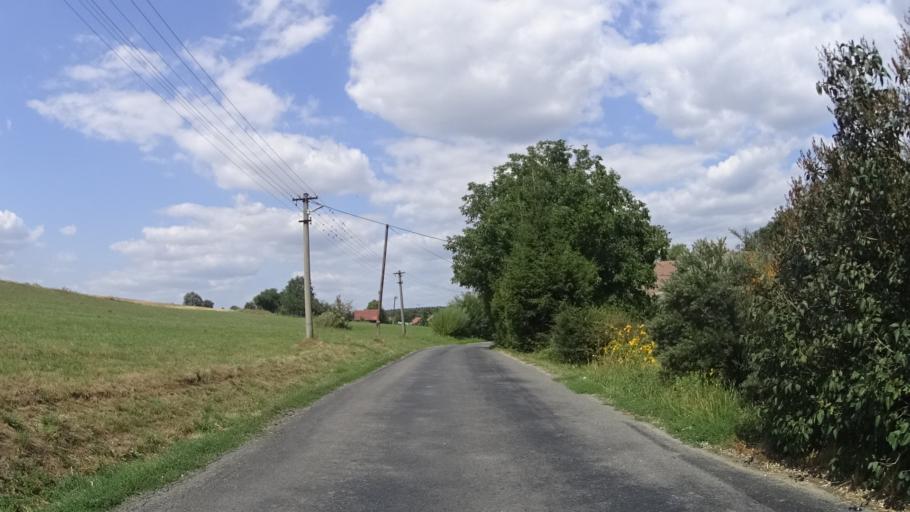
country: CZ
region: Kralovehradecky
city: Kopidlno
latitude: 50.3958
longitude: 15.2851
